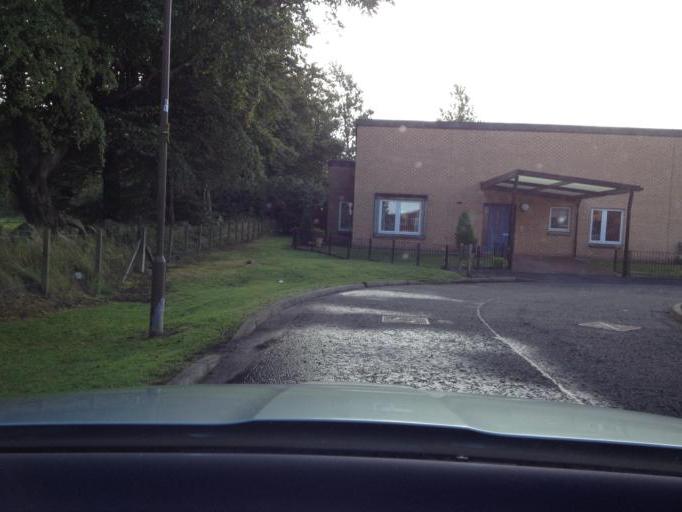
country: GB
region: Scotland
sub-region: West Lothian
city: Whitburn
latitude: 55.8677
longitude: -3.6681
